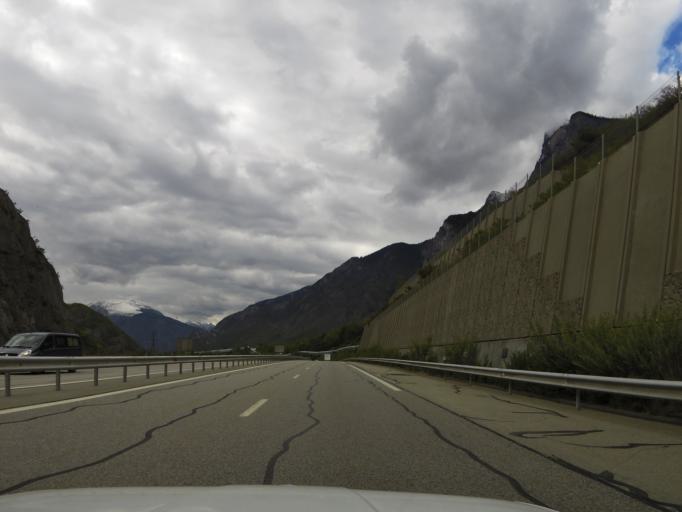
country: FR
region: Rhone-Alpes
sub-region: Departement de la Savoie
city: Saint-Michel-de-Maurienne
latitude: 45.2333
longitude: 6.4459
